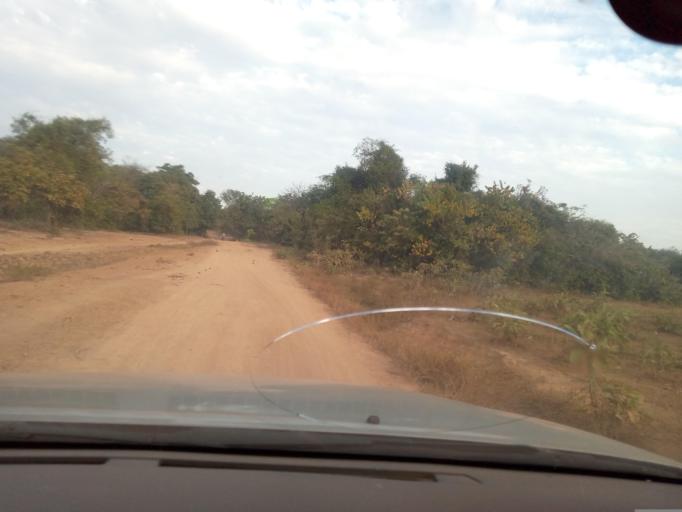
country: ML
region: Sikasso
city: Kadiolo
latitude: 10.5800
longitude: -5.8342
